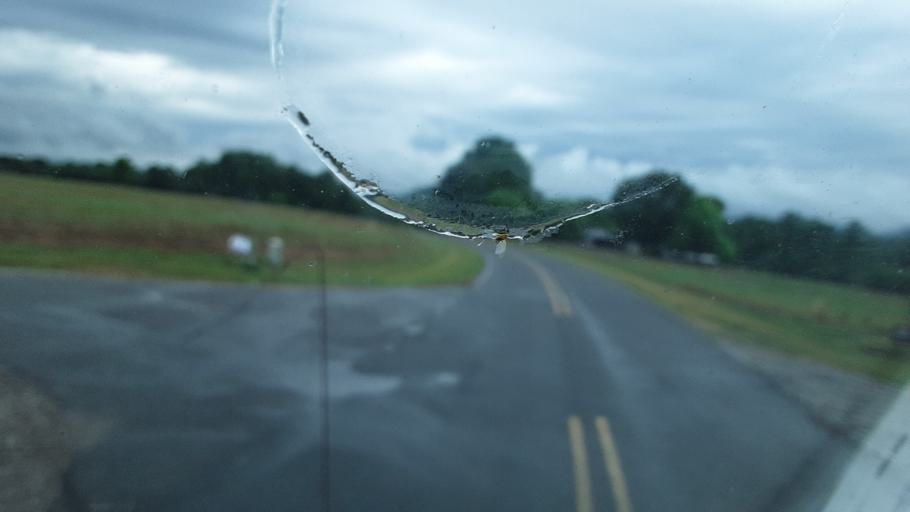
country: US
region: North Carolina
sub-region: Yadkin County
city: Jonesville
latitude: 36.0837
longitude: -80.8738
